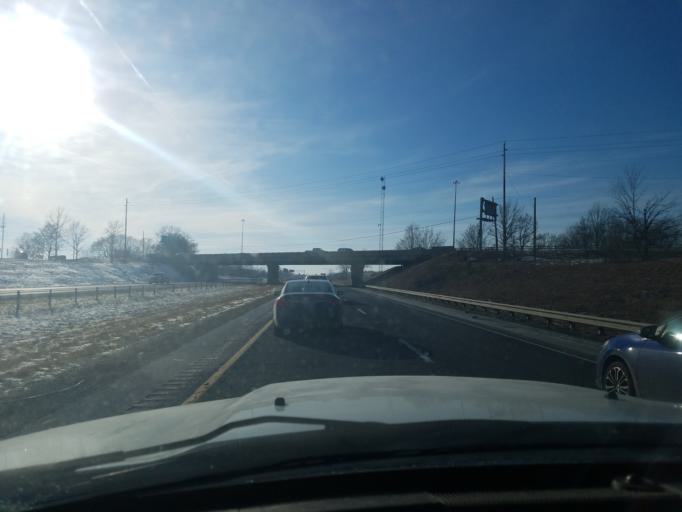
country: US
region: Indiana
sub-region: Madison County
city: Pendleton
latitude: 40.0383
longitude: -85.7204
